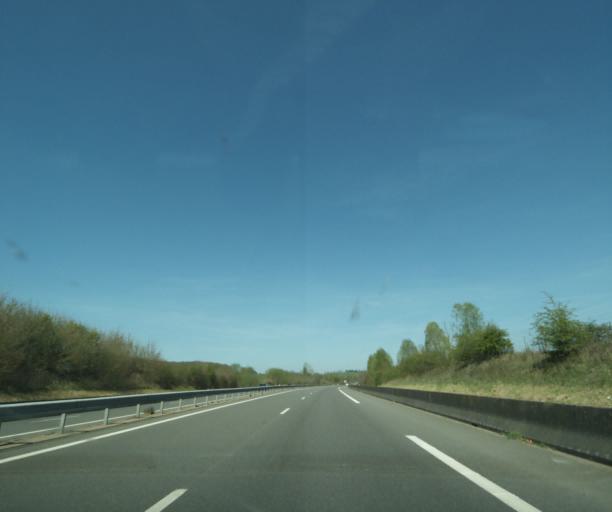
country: FR
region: Bourgogne
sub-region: Departement de la Nievre
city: Pougues-les-Eaux
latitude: 47.0646
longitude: 3.1296
